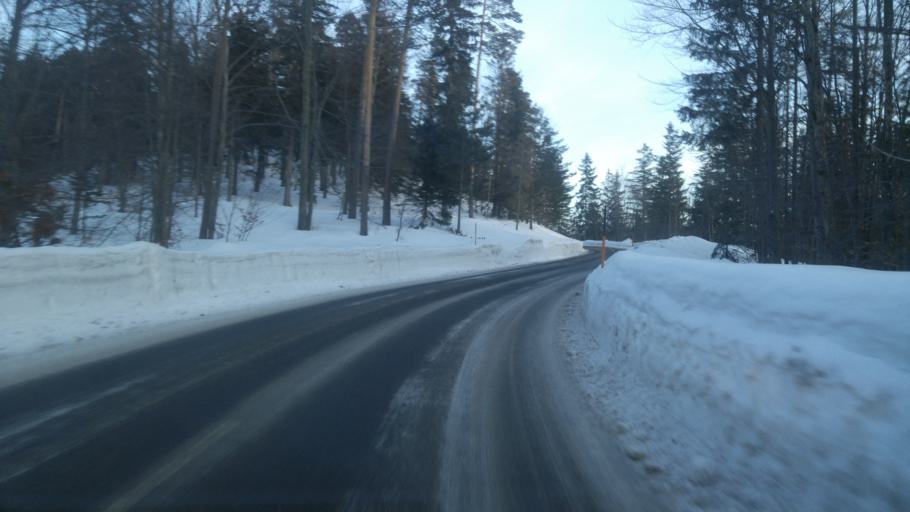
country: AT
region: Lower Austria
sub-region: Politischer Bezirk Lilienfeld
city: Hohenberg
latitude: 47.8840
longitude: 15.6413
